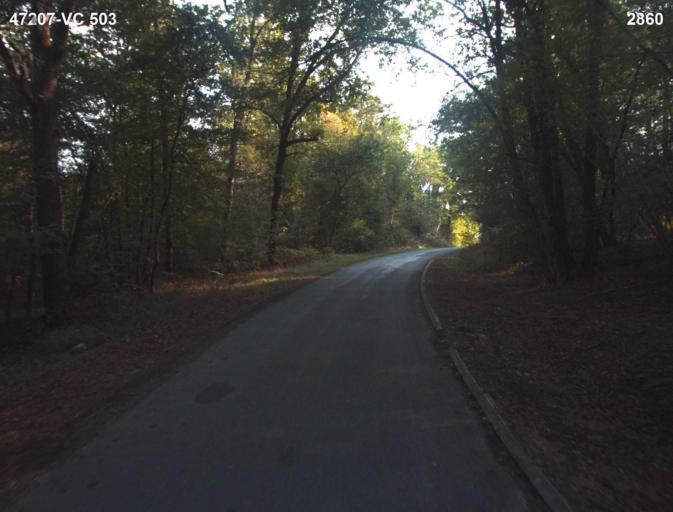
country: FR
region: Aquitaine
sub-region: Departement du Lot-et-Garonne
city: Barbaste
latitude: 44.1838
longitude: 0.2366
